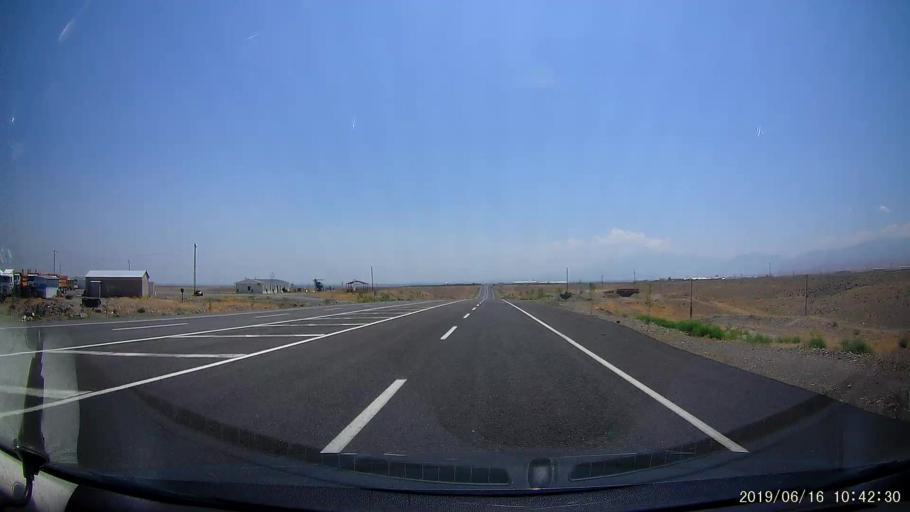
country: AM
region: Armavir
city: Shenavan
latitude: 40.0416
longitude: 43.8078
